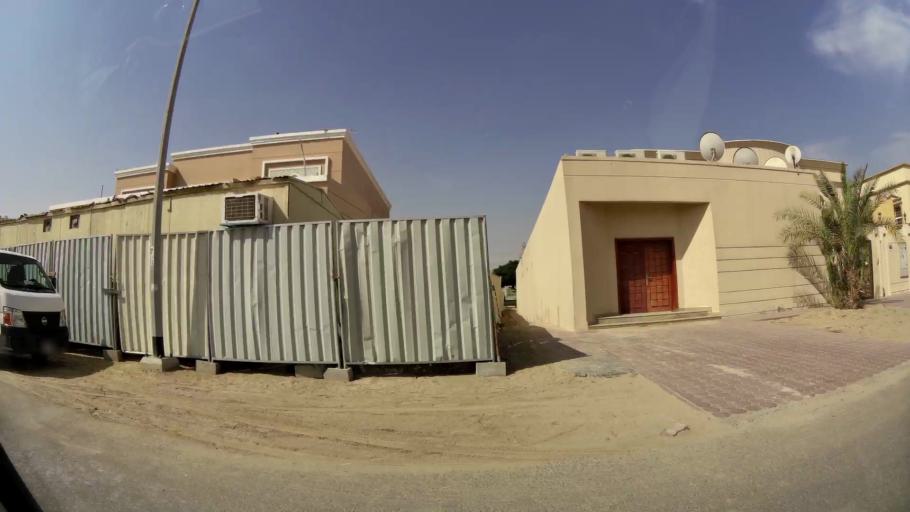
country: AE
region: Ash Shariqah
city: Sharjah
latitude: 25.2679
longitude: 55.4032
